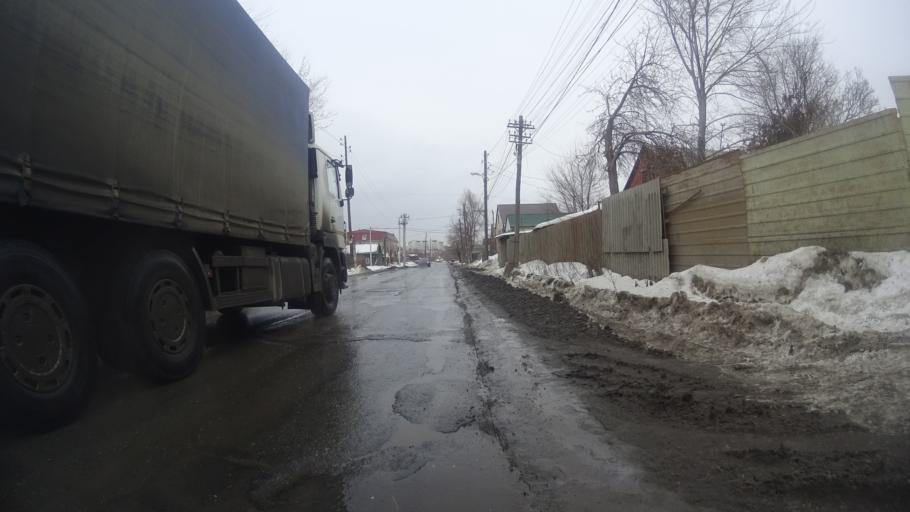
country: RU
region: Chelyabinsk
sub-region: Gorod Chelyabinsk
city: Chelyabinsk
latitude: 55.1291
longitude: 61.3938
